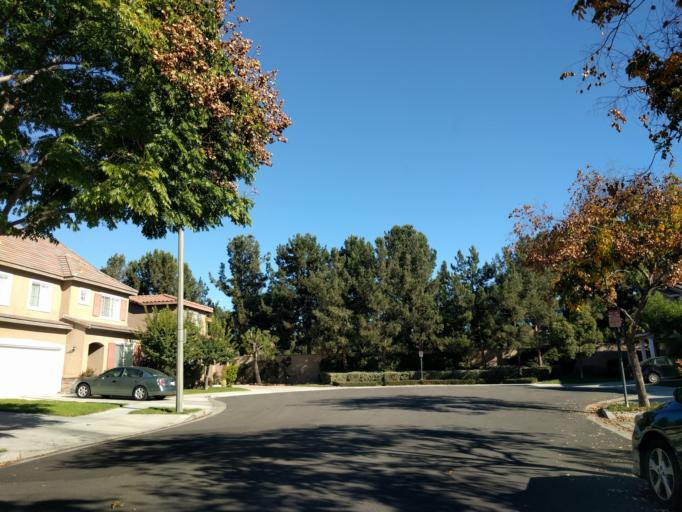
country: US
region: California
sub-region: Orange County
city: North Tustin
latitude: 33.7240
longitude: -117.7759
